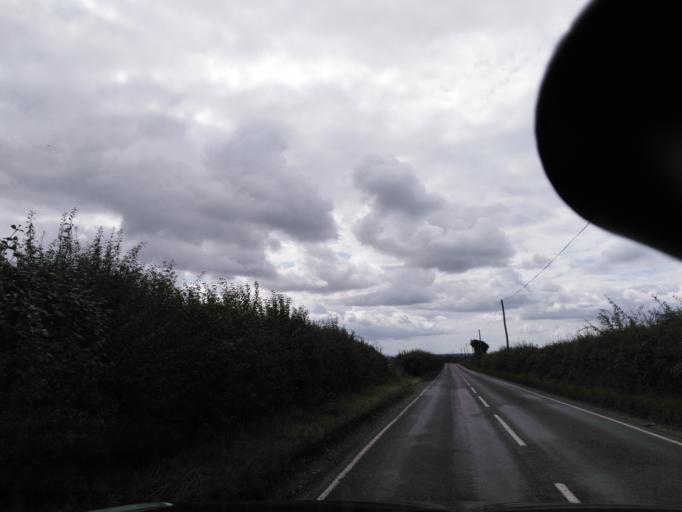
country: GB
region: England
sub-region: Dorset
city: Blandford Forum
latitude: 50.8827
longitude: -2.1588
